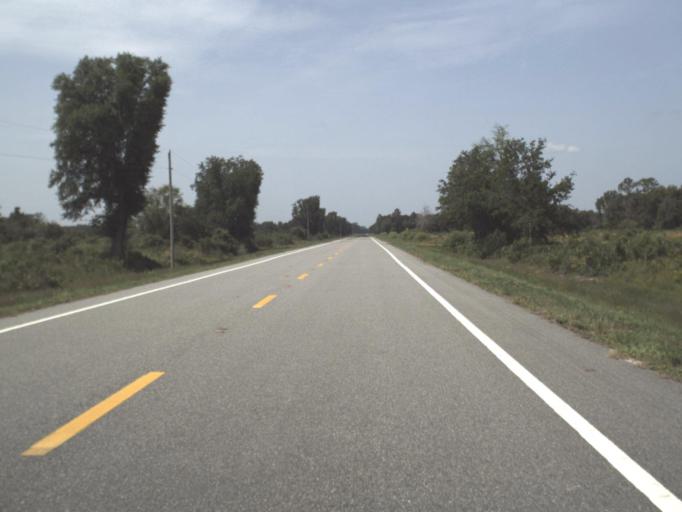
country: US
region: Florida
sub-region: Taylor County
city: Steinhatchee
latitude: 29.8075
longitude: -83.3184
